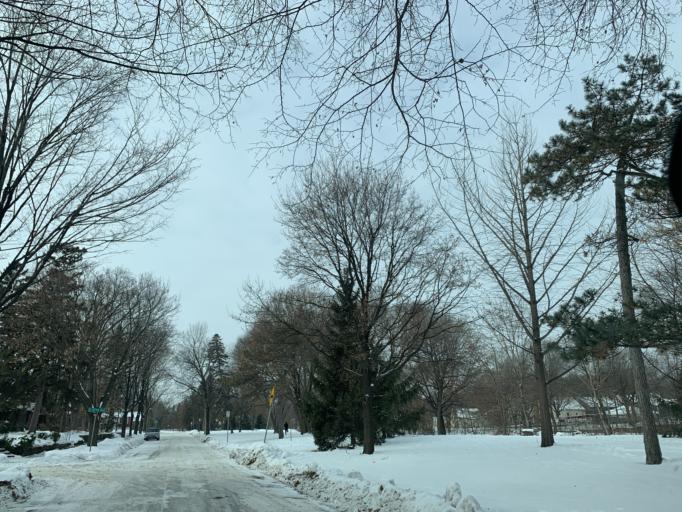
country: US
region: Minnesota
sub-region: Hennepin County
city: Richfield
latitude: 44.9180
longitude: -93.2186
